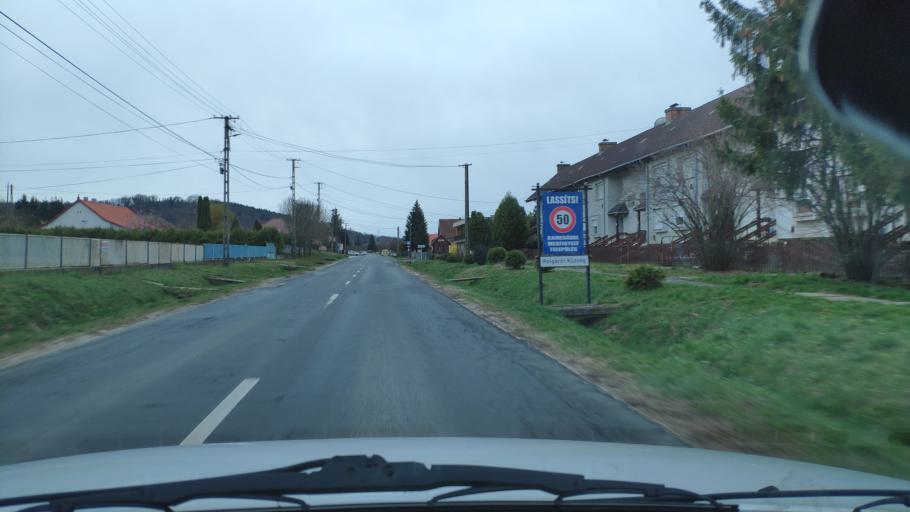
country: HU
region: Zala
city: Nagykanizsa
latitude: 46.5439
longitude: 16.9852
